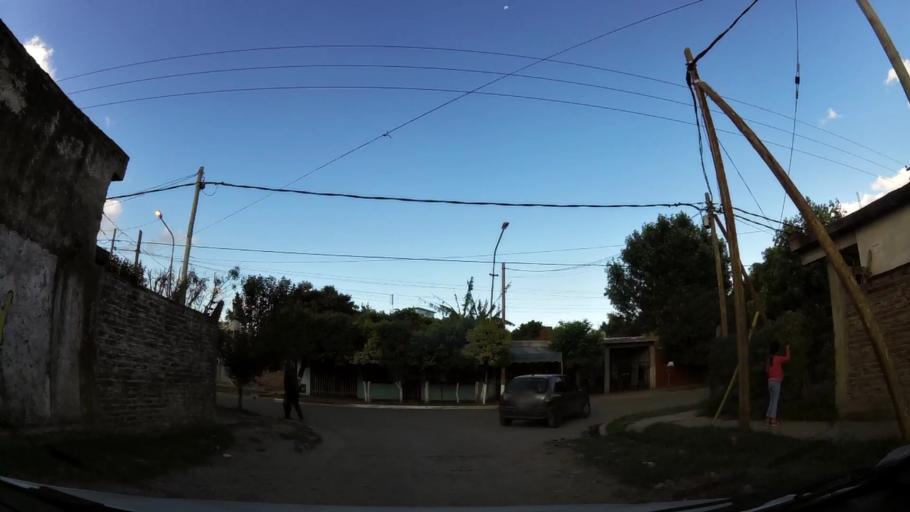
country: AR
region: Buenos Aires
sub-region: Partido de Moron
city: Moron
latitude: -34.7076
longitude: -58.6176
